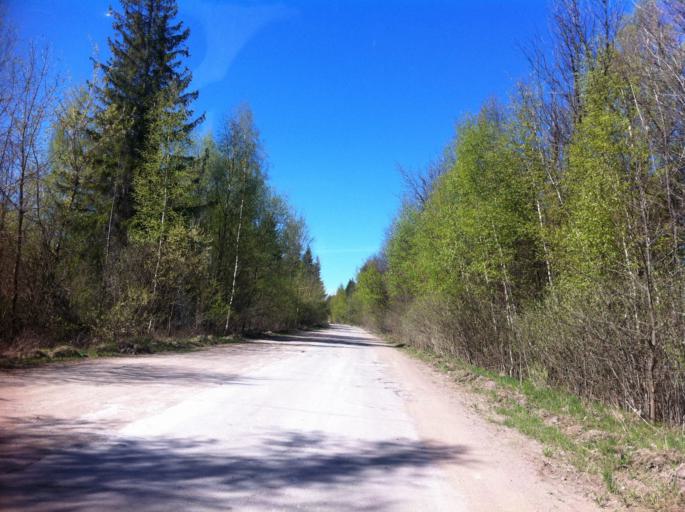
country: RU
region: Pskov
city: Izborsk
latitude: 57.7757
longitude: 27.9516
